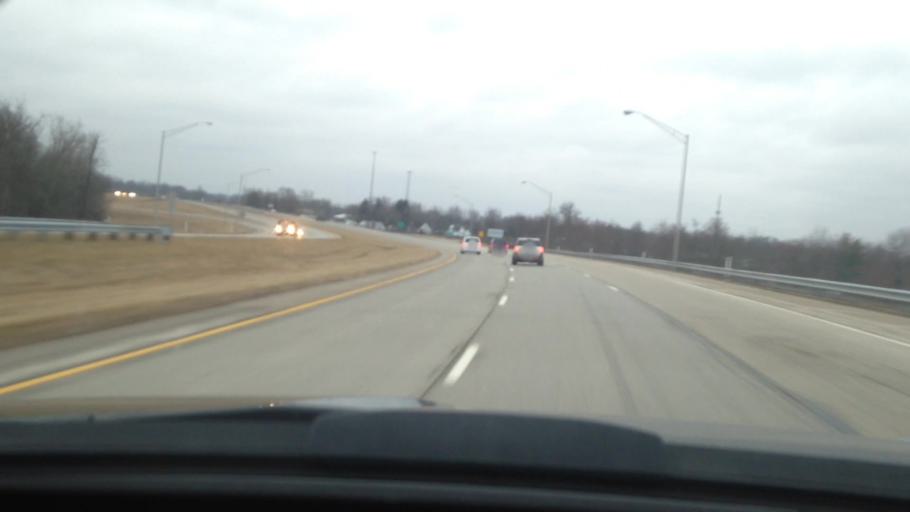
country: US
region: Indiana
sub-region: Delaware County
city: Muncie
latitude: 40.1650
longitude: -85.3523
